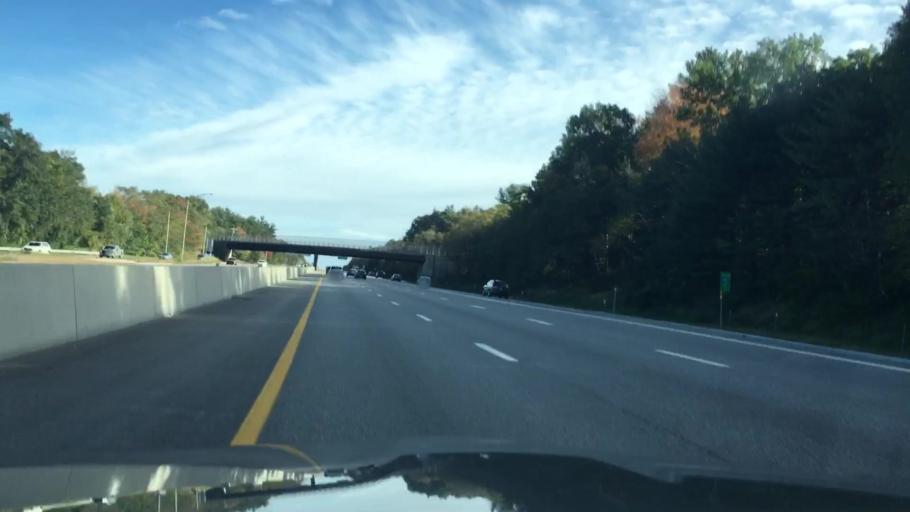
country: US
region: New Hampshire
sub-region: Merrimack County
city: Concord
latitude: 43.1675
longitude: -71.5272
